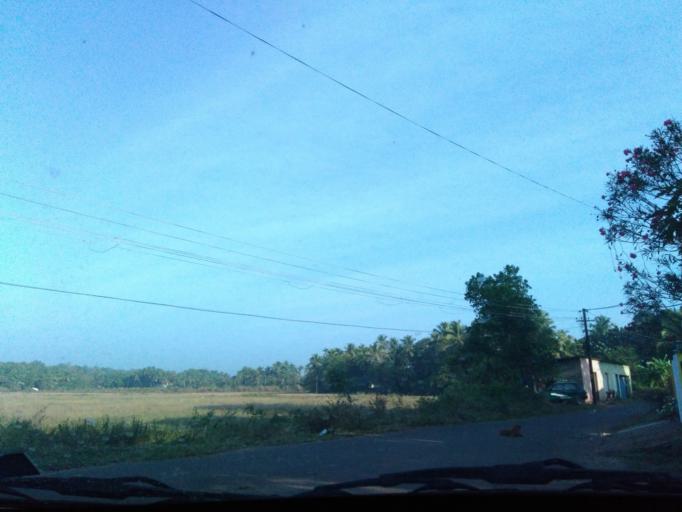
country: IN
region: Goa
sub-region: South Goa
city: Chinchinim
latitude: 15.2117
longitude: 73.9707
